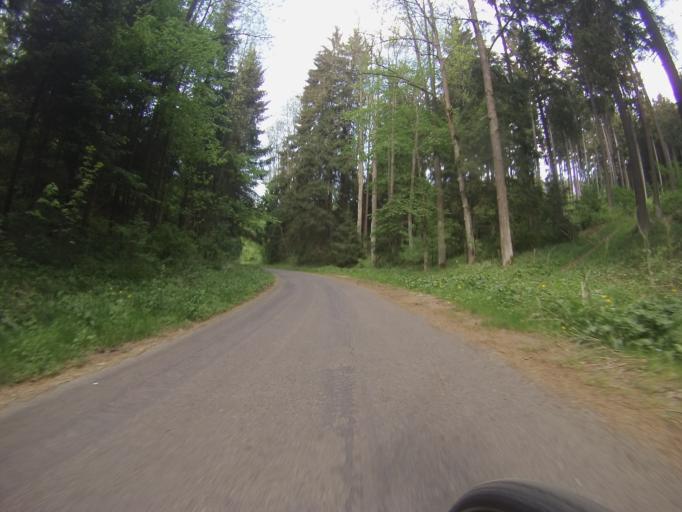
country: CZ
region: South Moravian
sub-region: Okres Blansko
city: Jedovnice
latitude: 49.3669
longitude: 16.7312
